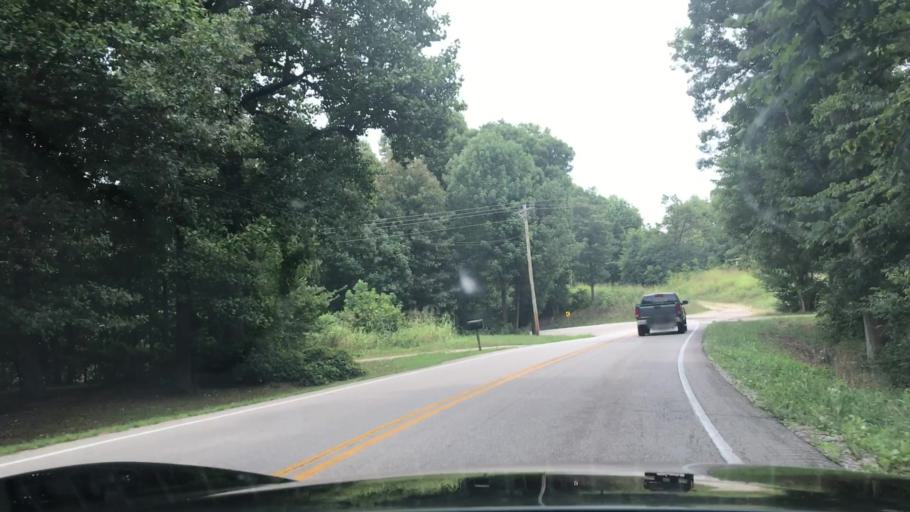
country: US
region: Kentucky
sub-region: Butler County
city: Morgantown
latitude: 37.2078
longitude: -86.7270
